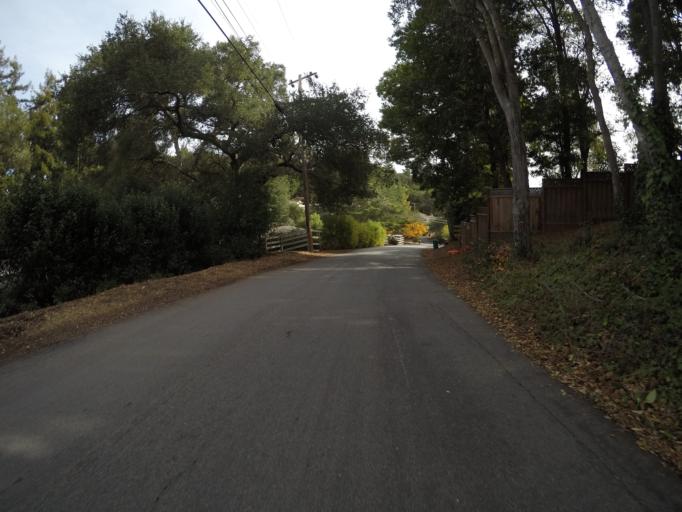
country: US
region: California
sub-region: Santa Cruz County
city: Scotts Valley
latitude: 37.0604
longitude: -121.9936
